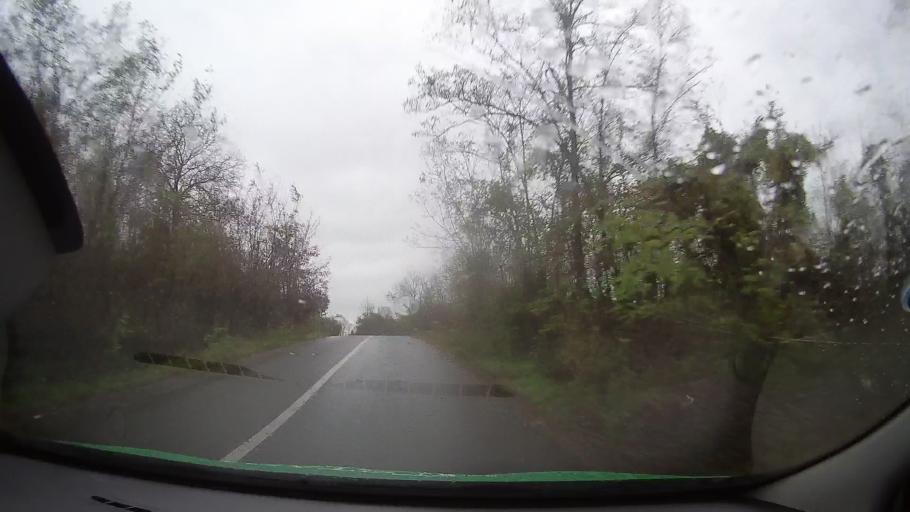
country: RO
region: Mures
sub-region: Comuna Brancovenesti
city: Valenii de Mures
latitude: 46.8980
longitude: 24.7949
